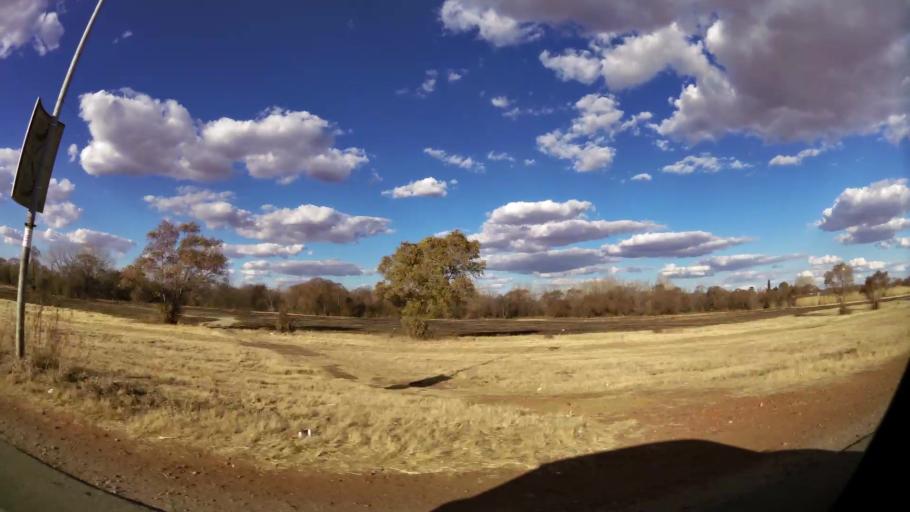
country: ZA
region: North-West
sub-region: Dr Kenneth Kaunda District Municipality
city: Potchefstroom
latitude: -26.7022
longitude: 27.1046
